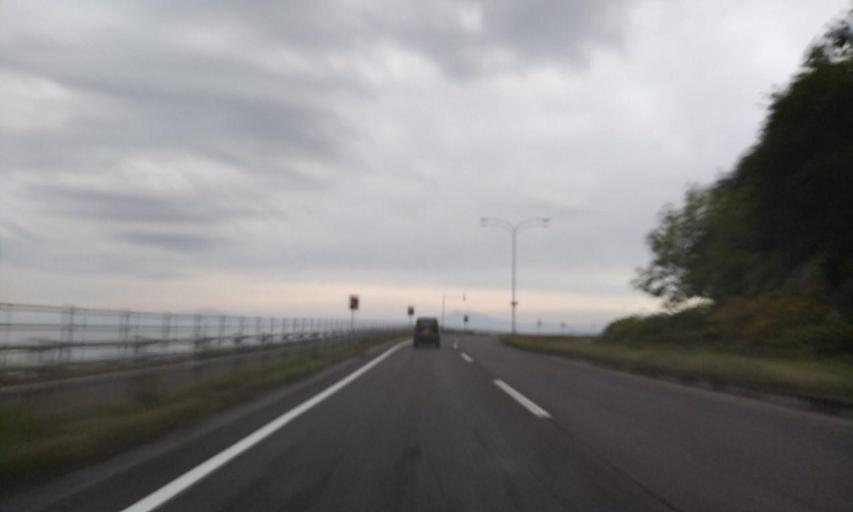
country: JP
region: Hokkaido
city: Abashiri
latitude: 44.0023
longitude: 144.2884
